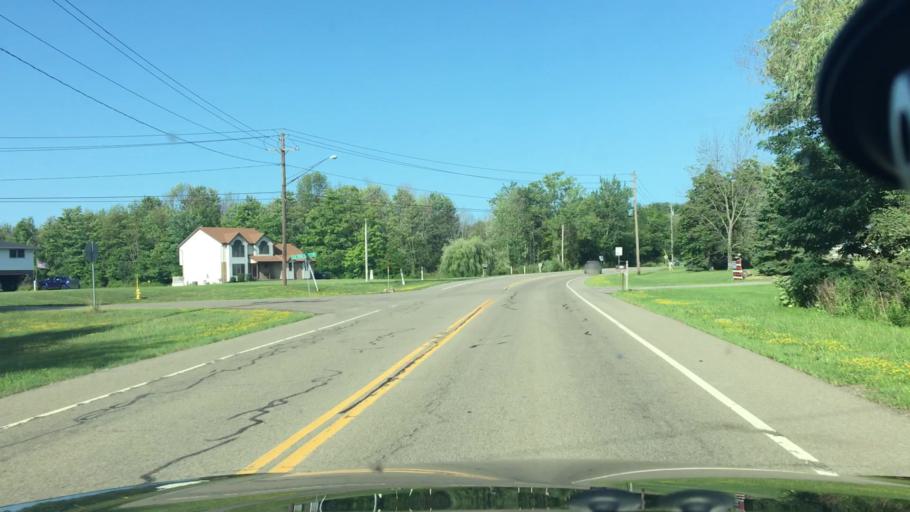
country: US
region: New York
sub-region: Erie County
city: Angola
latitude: 42.6520
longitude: -79.0259
